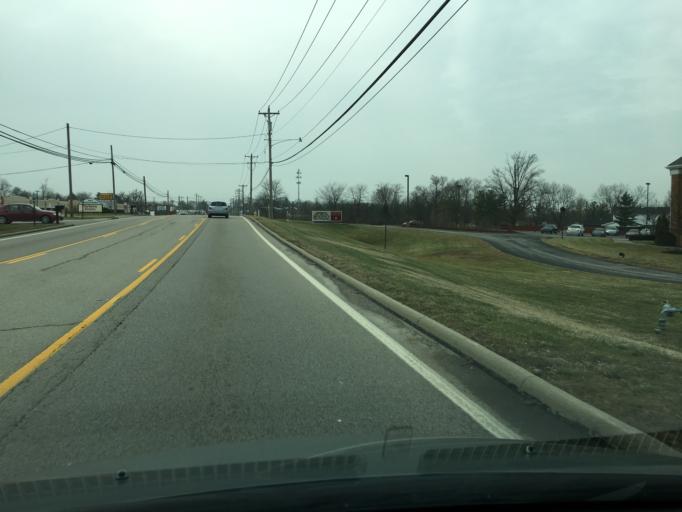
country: US
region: Ohio
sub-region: Hamilton County
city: Highpoint
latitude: 39.3137
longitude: -84.3760
